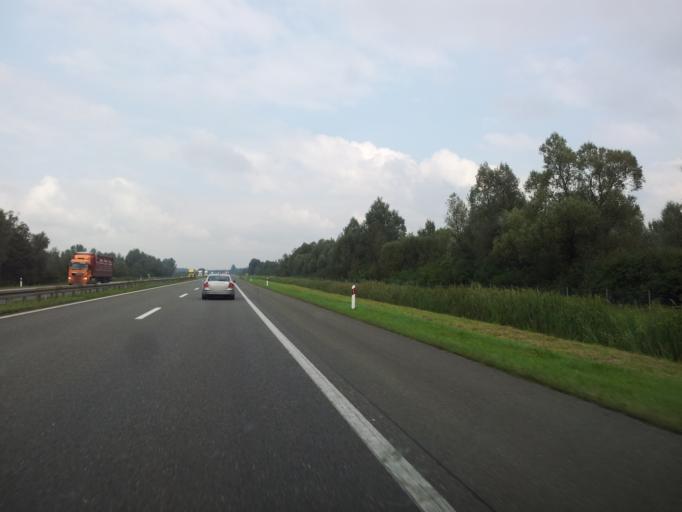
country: HR
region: Zagrebacka
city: Novoselec
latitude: 45.5889
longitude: 16.5580
